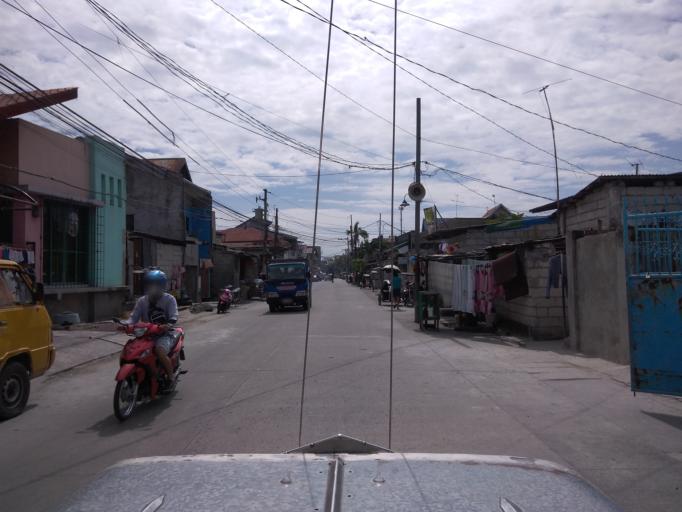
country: PH
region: Central Luzon
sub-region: Province of Pampanga
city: Sexmoan
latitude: 14.9393
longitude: 120.6212
